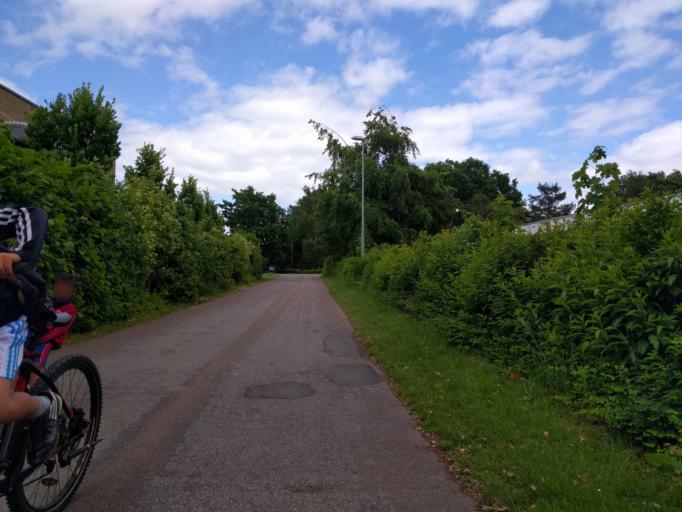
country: DK
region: South Denmark
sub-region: Odense Kommune
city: Seden
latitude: 55.4051
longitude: 10.4366
